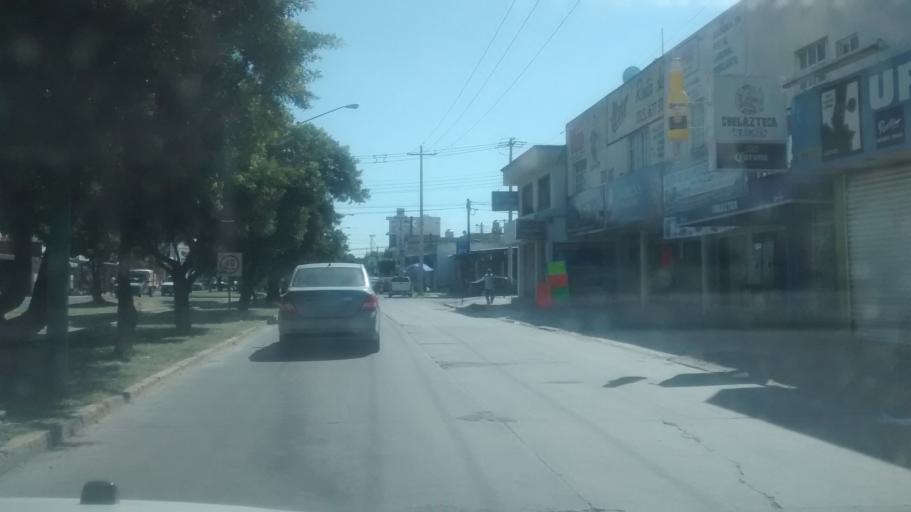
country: MX
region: Guanajuato
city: Leon
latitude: 21.1022
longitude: -101.6539
